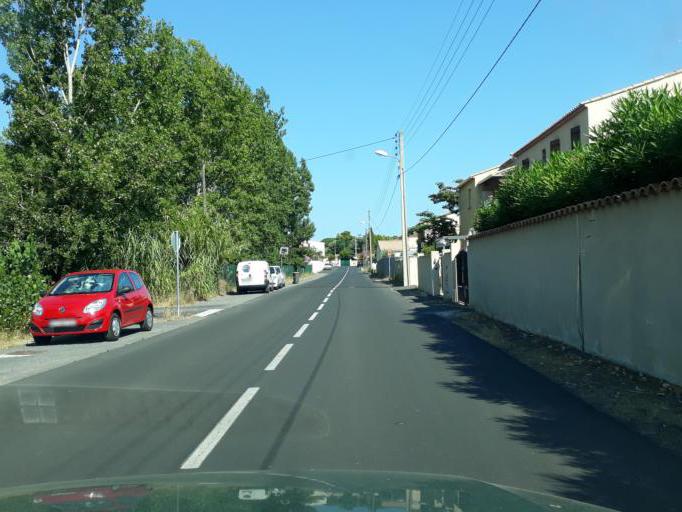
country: FR
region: Languedoc-Roussillon
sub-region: Departement de l'Herault
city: Agde
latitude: 43.2912
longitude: 3.4529
